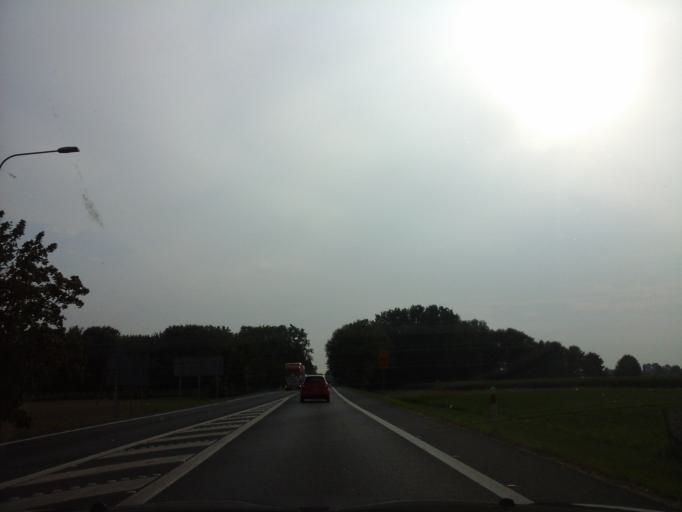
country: PL
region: Greater Poland Voivodeship
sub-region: Powiat koscianski
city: Koscian
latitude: 52.0977
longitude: 16.6412
